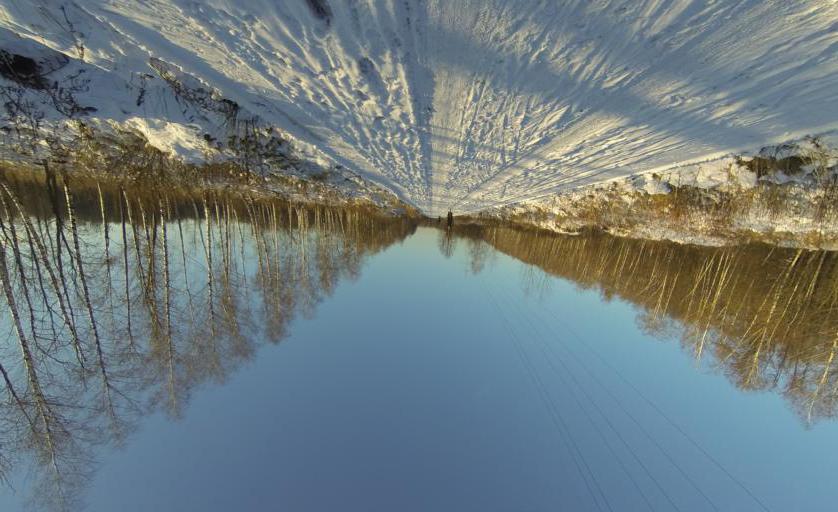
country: RU
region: Moscow
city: Babushkin
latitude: 55.8428
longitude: 37.7544
